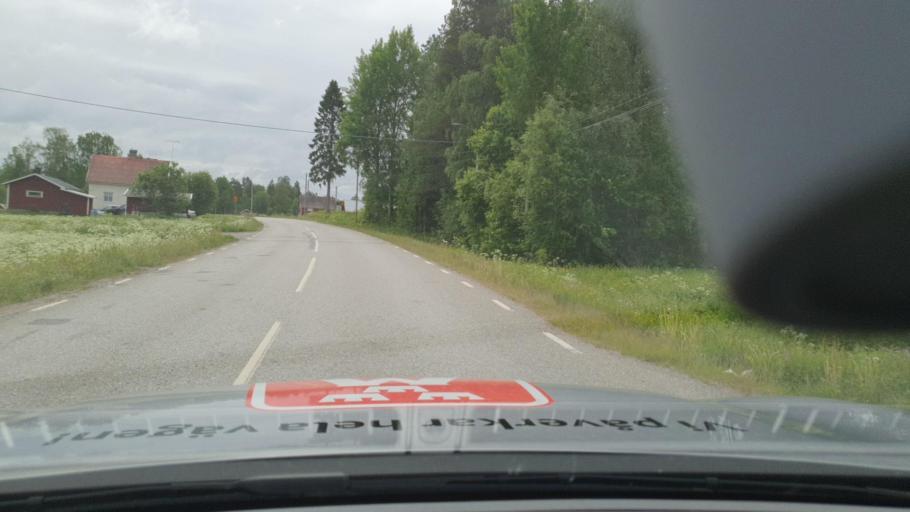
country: SE
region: Norrbotten
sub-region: Lulea Kommun
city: Ranea
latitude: 65.9196
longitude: 22.1505
